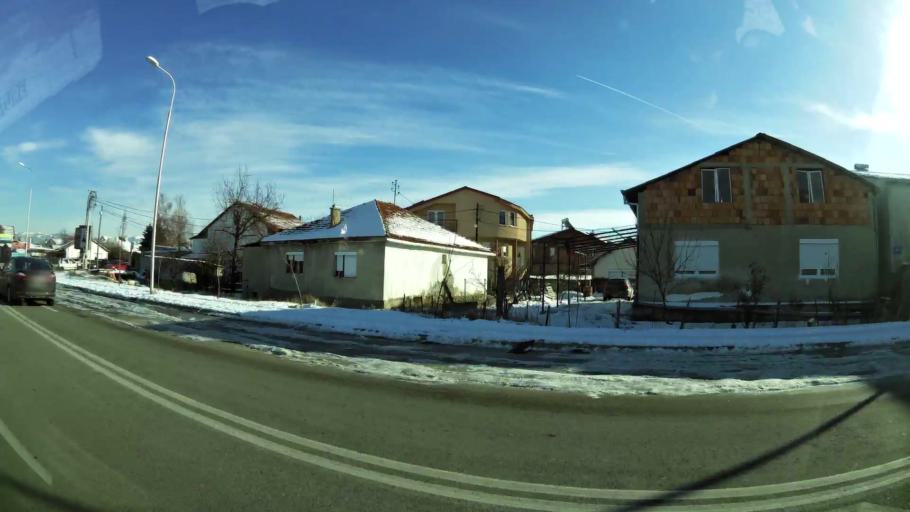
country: MK
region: Saraj
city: Saraj
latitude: 42.0054
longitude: 21.3447
